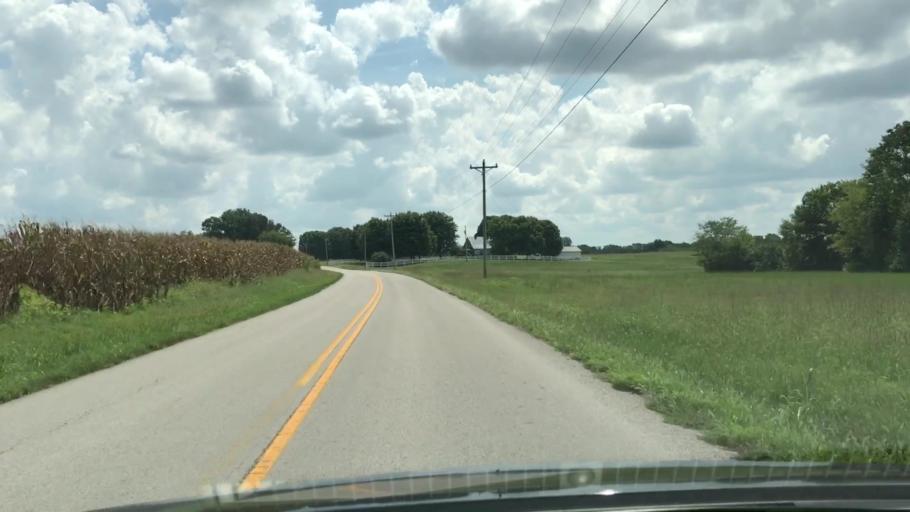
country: US
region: Kentucky
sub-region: Todd County
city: Elkton
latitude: 36.7895
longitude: -87.1358
